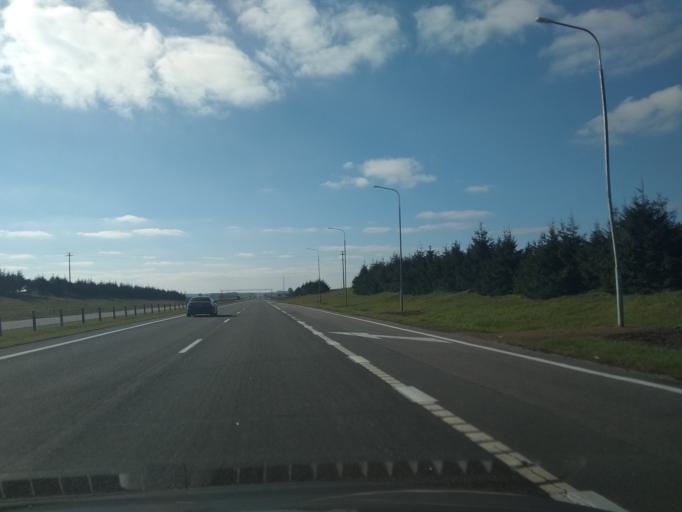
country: BY
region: Minsk
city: Haradzyeya
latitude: 53.3547
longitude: 26.4648
